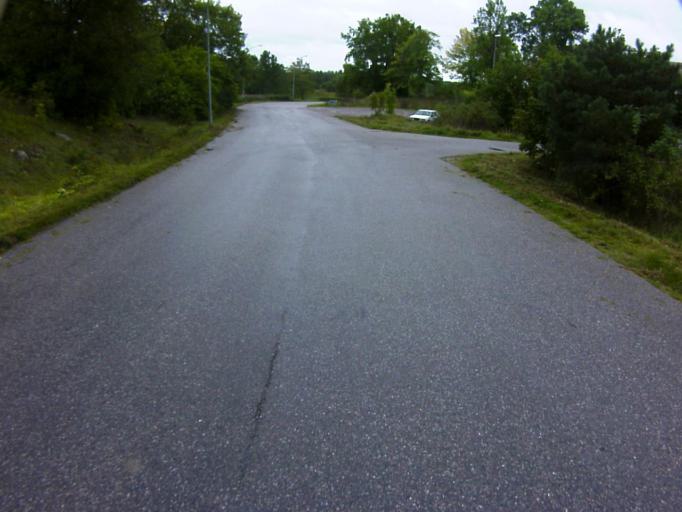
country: SE
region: Soedermanland
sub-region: Eskilstuna Kommun
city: Eskilstuna
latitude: 59.3864
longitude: 16.5402
